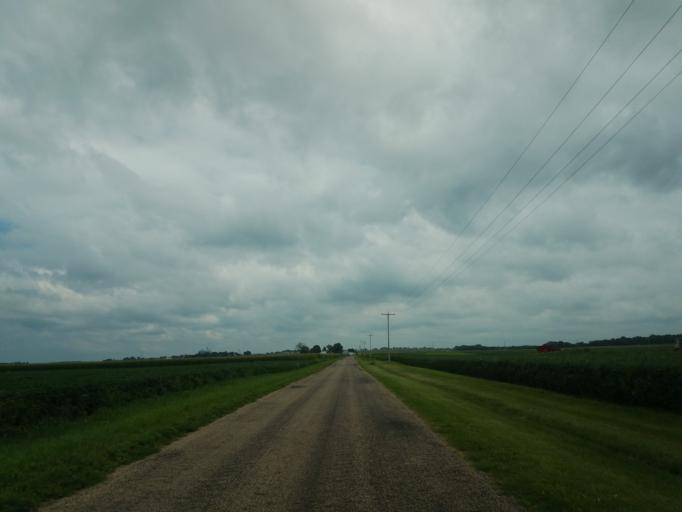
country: US
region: Illinois
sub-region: McLean County
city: Twin Grove
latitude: 40.4324
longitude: -89.0624
